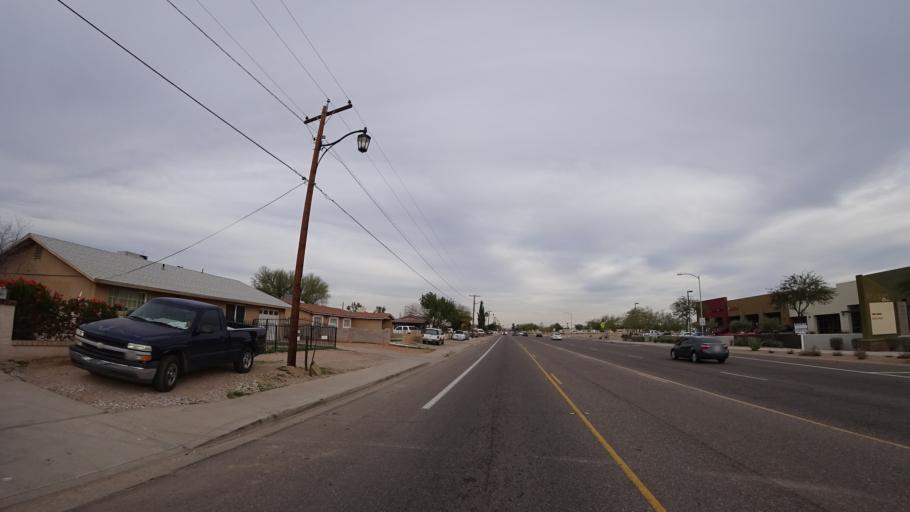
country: US
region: Arizona
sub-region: Maricopa County
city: Surprise
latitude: 33.6236
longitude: -112.3404
